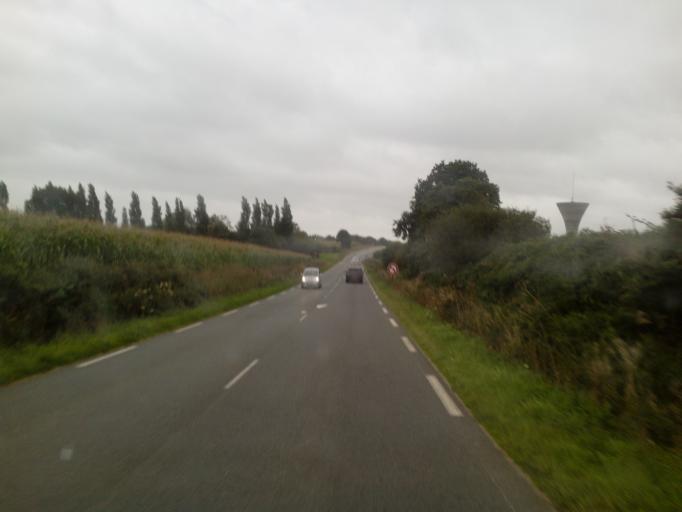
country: FR
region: Brittany
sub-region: Departement des Cotes-d'Armor
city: Plehedel
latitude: 48.7216
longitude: -3.0244
